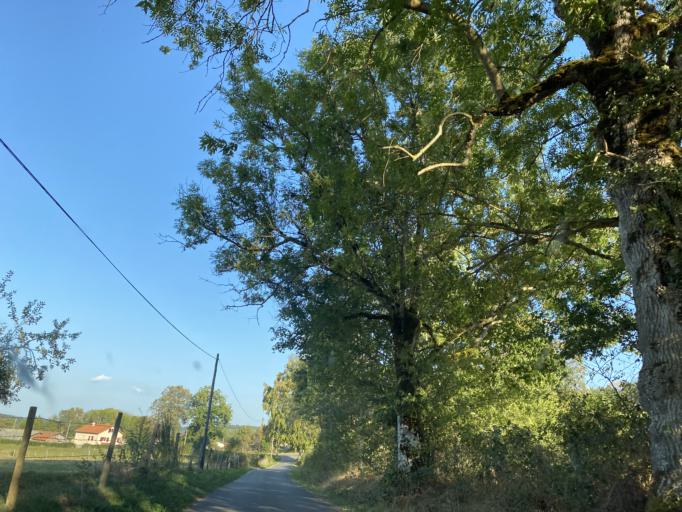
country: FR
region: Rhone-Alpes
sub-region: Departement de la Loire
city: Noiretable
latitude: 45.7998
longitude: 3.7638
